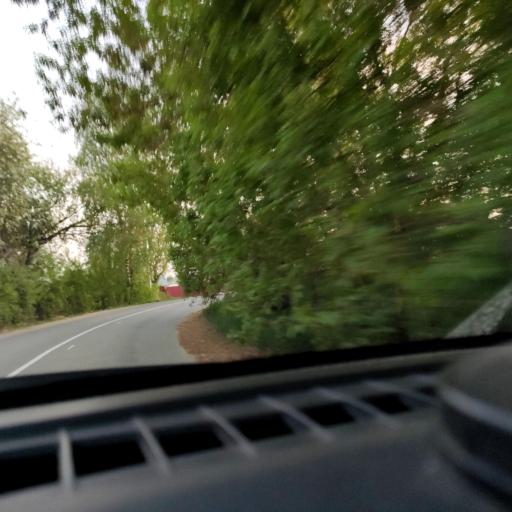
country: RU
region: Perm
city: Kultayevo
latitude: 57.9350
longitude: 55.8818
